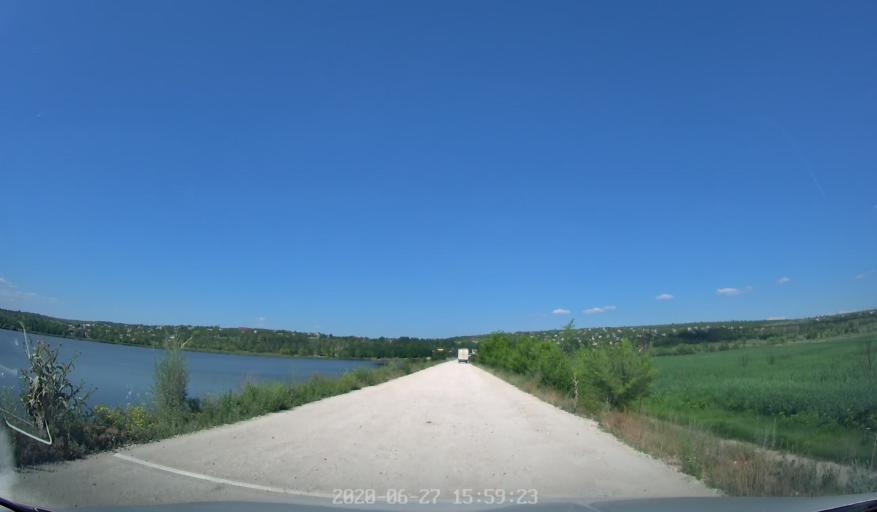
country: MD
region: Laloveni
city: Ialoveni
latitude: 46.9773
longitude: 28.6988
